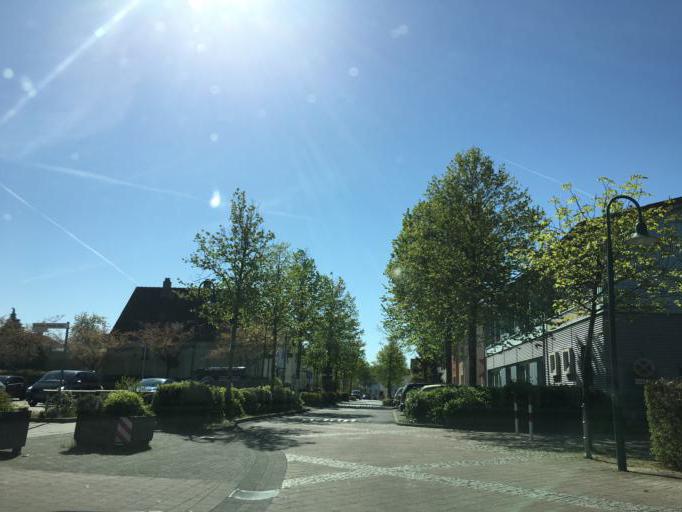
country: DE
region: Hesse
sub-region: Regierungsbezirk Darmstadt
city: Eppertshausen
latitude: 49.9478
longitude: 8.8478
